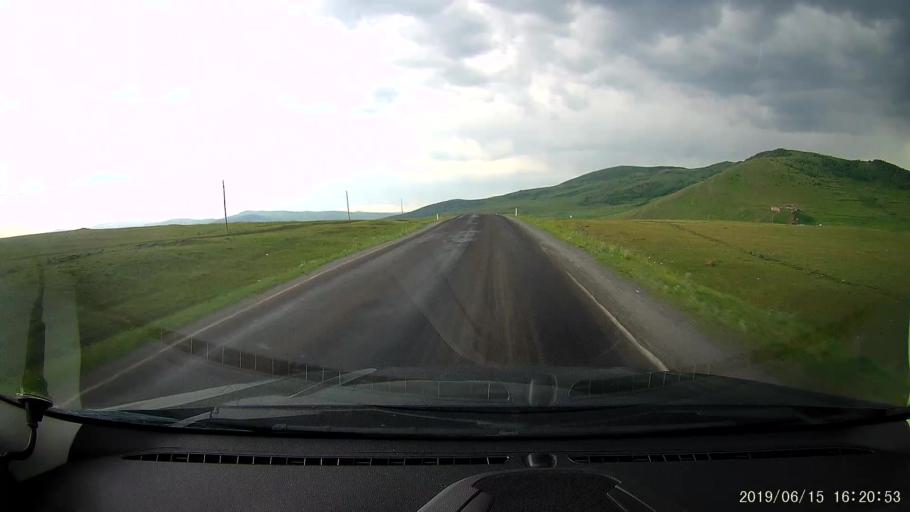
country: TR
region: Ardahan
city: Hanak
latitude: 41.2063
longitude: 42.8464
